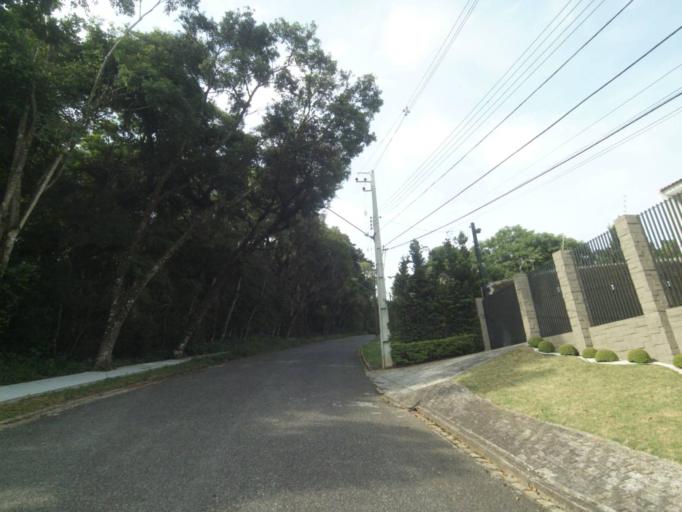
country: BR
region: Parana
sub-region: Curitiba
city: Curitiba
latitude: -25.4124
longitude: -49.3157
